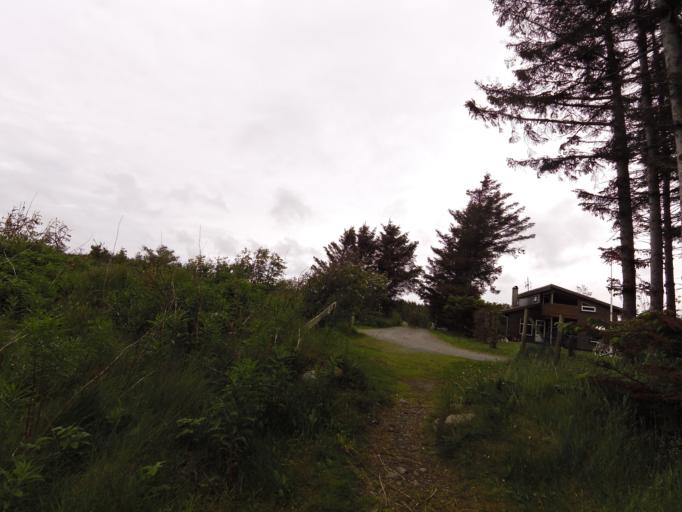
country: NO
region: Rogaland
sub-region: Ha
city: Naerbo
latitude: 58.6943
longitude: 5.5488
